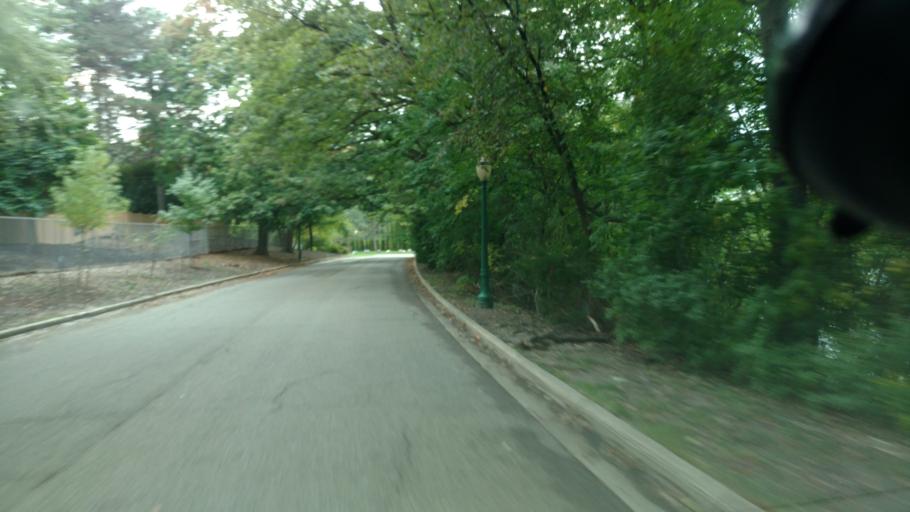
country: US
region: Michigan
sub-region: Ingham County
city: Edgemont Park
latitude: 42.7202
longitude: -84.5857
